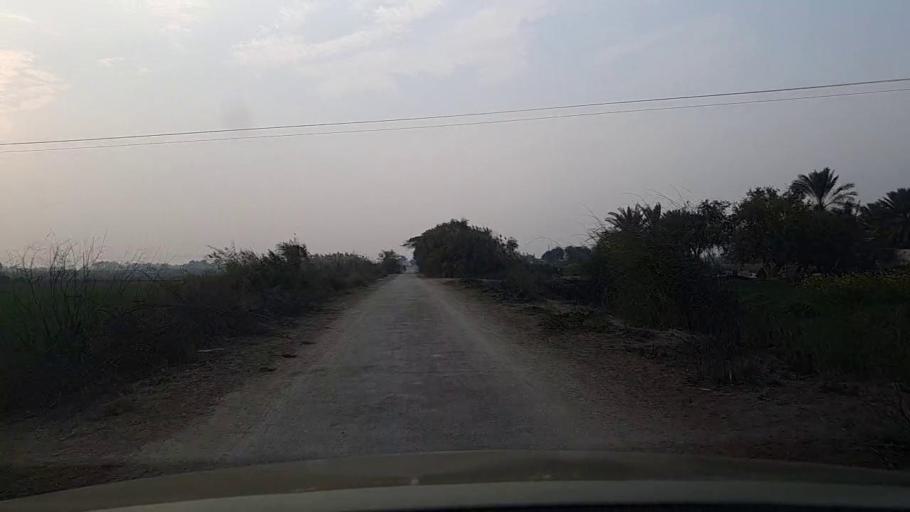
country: PK
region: Sindh
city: Sanghar
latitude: 26.1857
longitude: 68.9583
